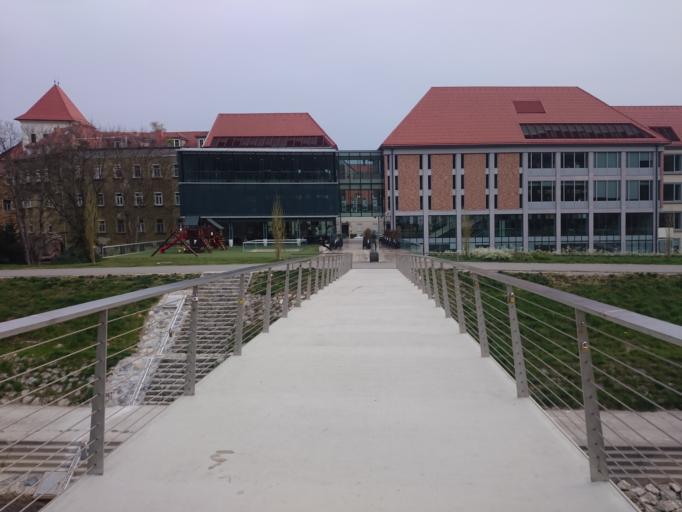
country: SI
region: Celje
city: Celje
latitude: 46.2274
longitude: 15.2606
